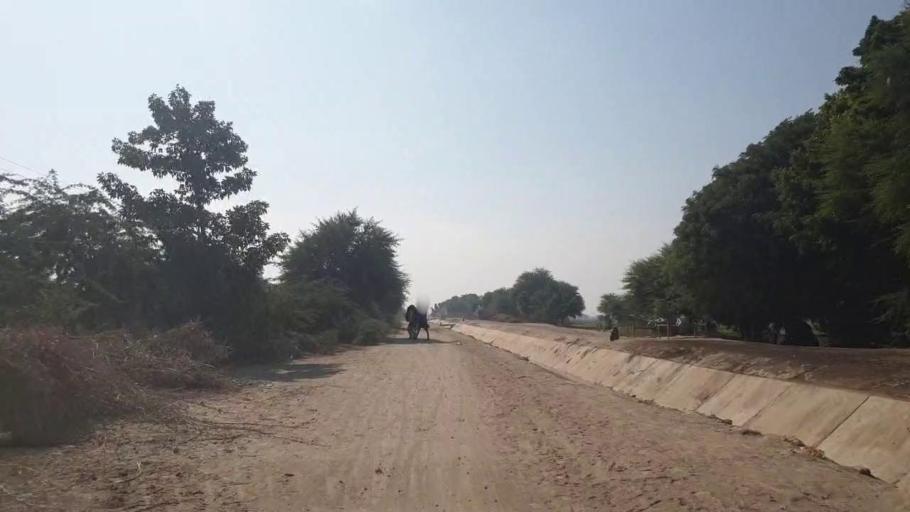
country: PK
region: Sindh
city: Matiari
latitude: 25.6722
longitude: 68.3489
